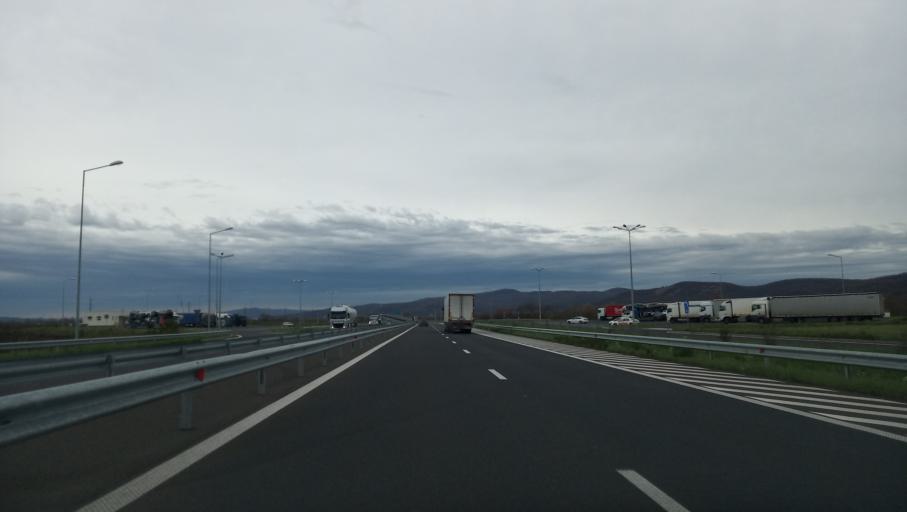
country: RO
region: Hunedoara
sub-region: Comuna Ilia
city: Ilia
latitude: 45.9478
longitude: 22.6552
